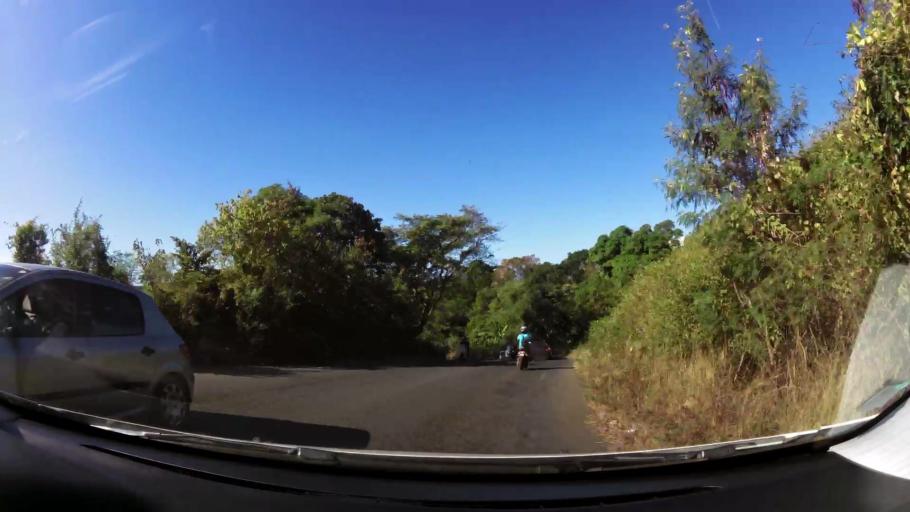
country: YT
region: Mamoudzou
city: Mamoudzou
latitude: -12.7776
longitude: 45.2255
